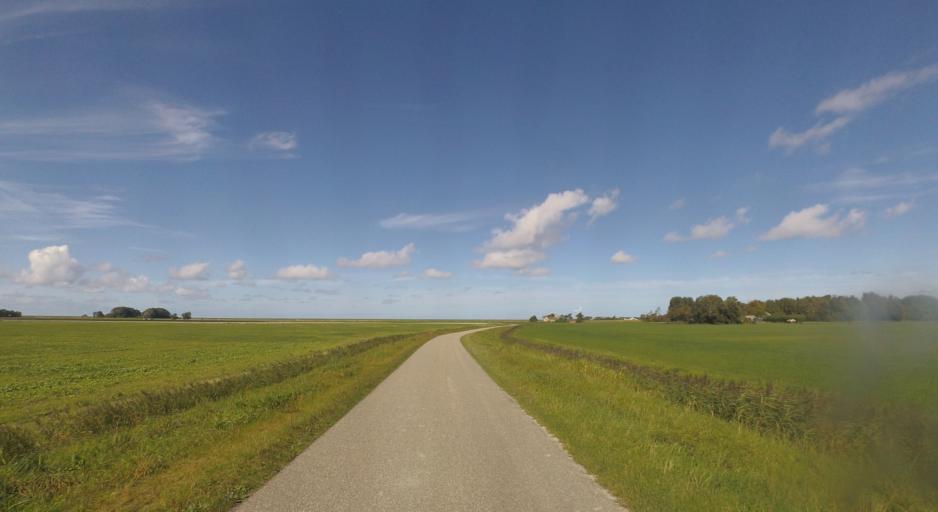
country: NL
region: Friesland
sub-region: Gemeente Dongeradeel
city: Holwerd
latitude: 53.3615
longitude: 5.8964
